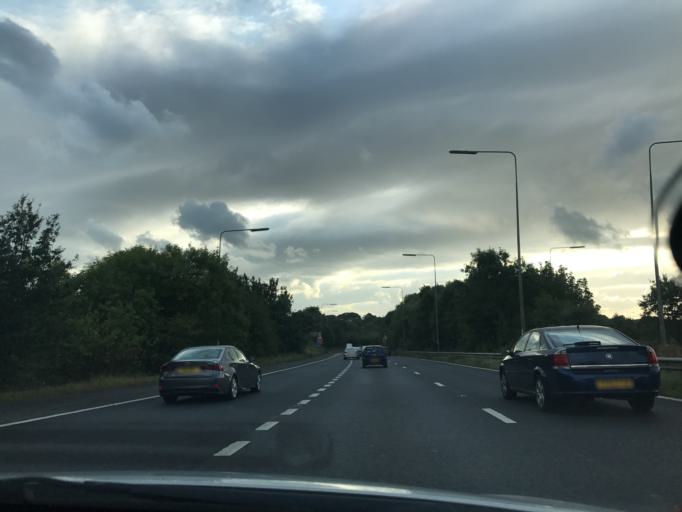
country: GB
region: England
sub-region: Cheshire West and Chester
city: Ledsham
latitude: 53.3035
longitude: -2.9645
